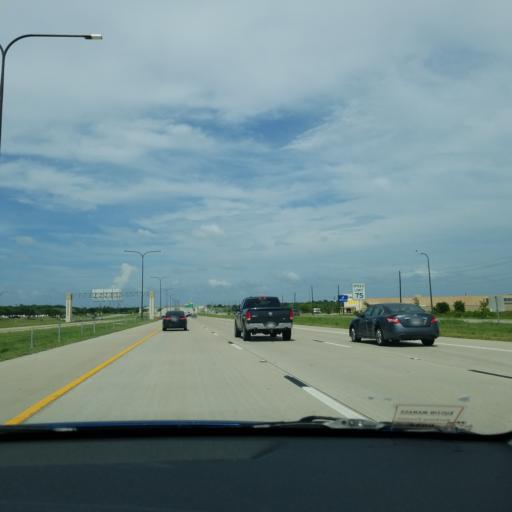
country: US
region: Texas
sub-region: Travis County
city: Manor
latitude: 30.3318
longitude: -97.6178
